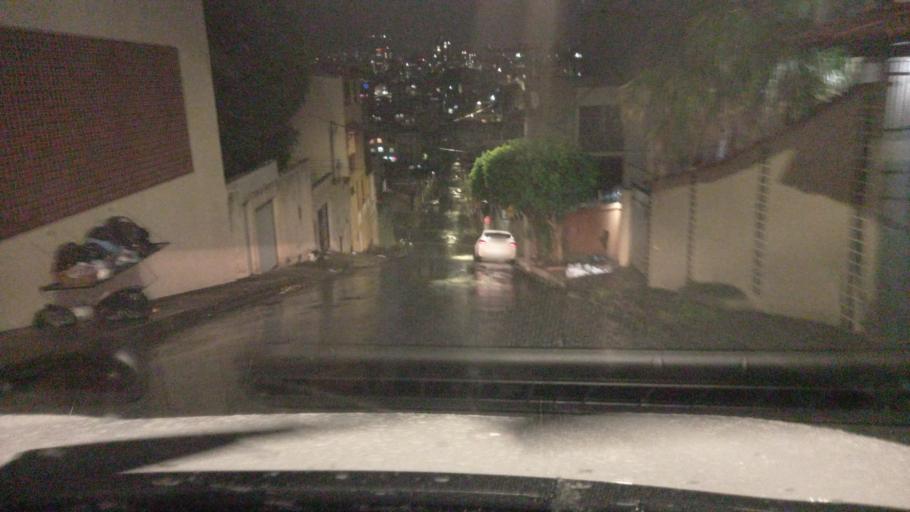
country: BR
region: Minas Gerais
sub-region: Belo Horizonte
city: Belo Horizonte
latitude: -19.9019
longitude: -43.9178
